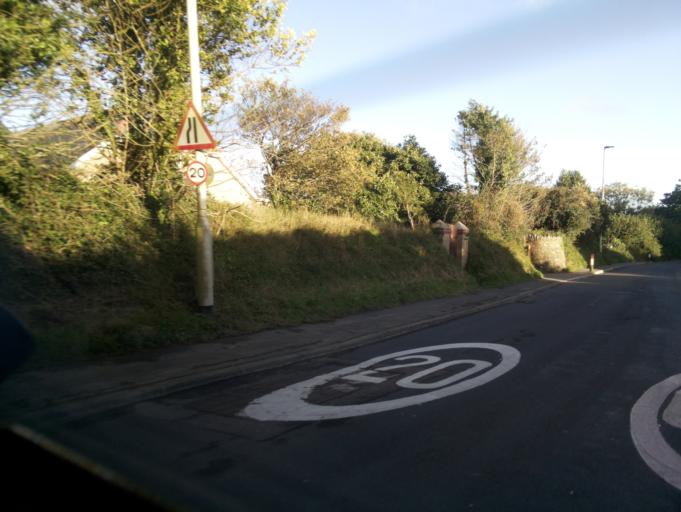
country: GB
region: England
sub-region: Devon
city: Dartmouth
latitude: 50.3283
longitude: -3.5976
